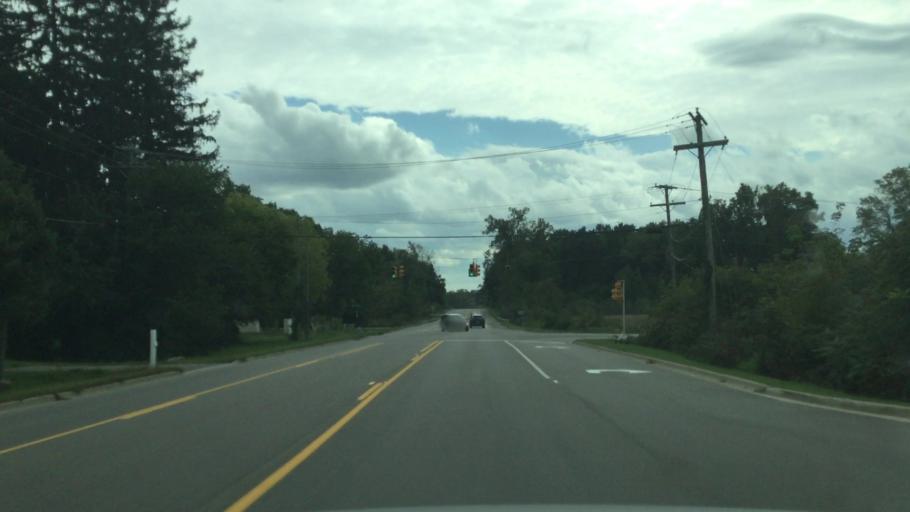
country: US
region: Michigan
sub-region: Livingston County
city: Brighton
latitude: 42.5530
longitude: -83.7532
